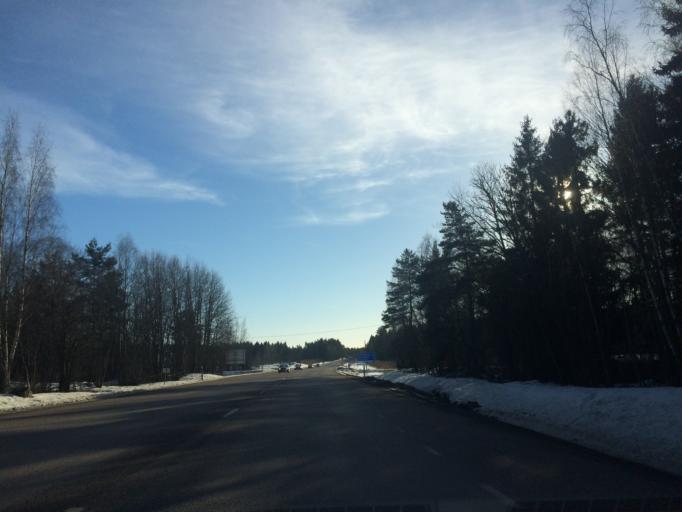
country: SE
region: Vaestmanland
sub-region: Hallstahammars Kommun
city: Kolback
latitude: 59.5766
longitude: 16.3529
